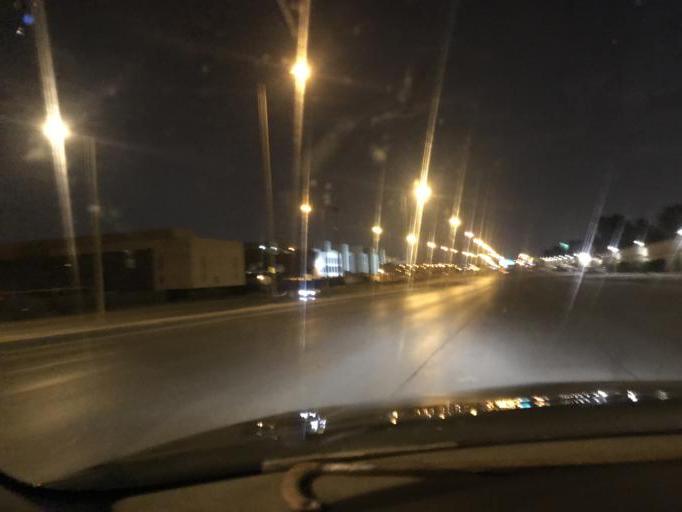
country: SA
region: Ar Riyad
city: Riyadh
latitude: 24.8126
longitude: 46.6903
